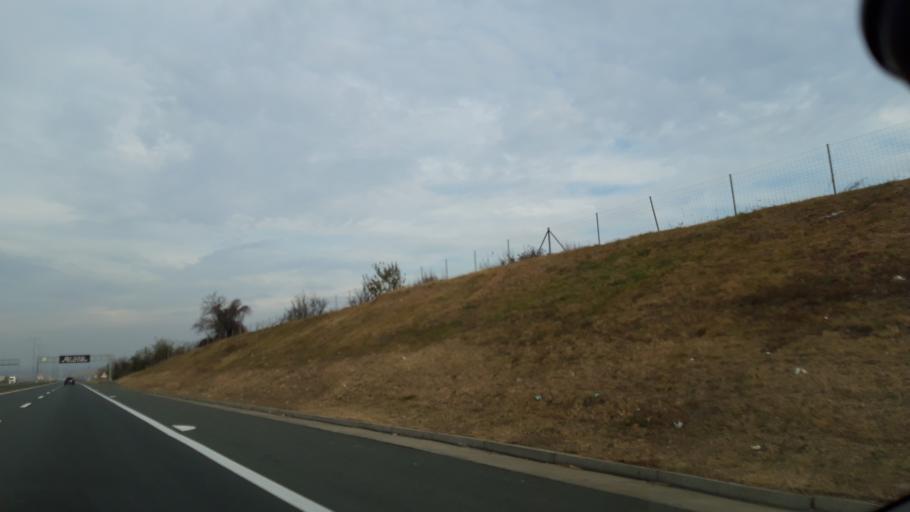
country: RS
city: Beska
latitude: 45.1611
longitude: 20.0813
